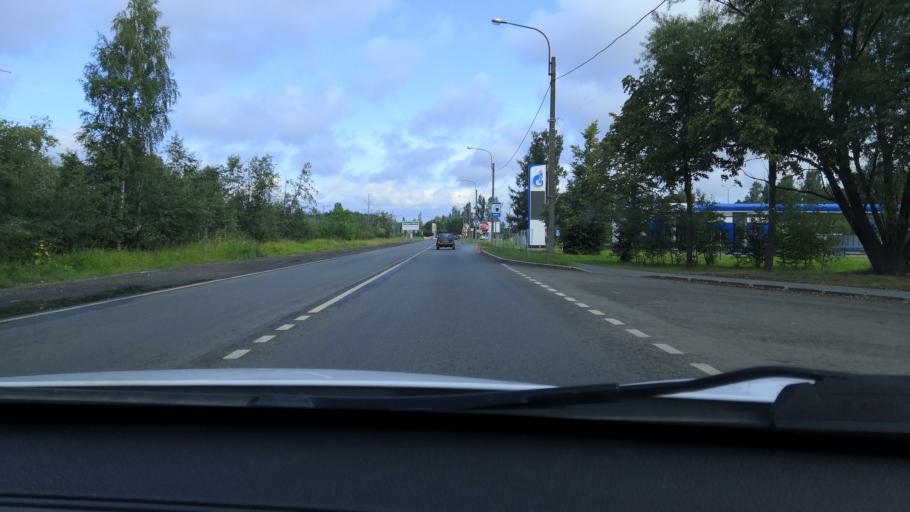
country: RU
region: St.-Petersburg
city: Tyarlevo
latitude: 59.7102
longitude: 30.4366
